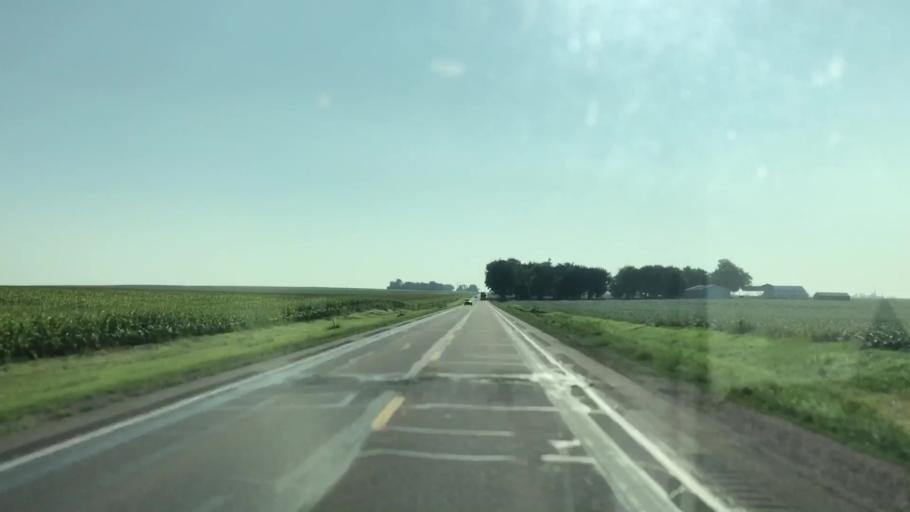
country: US
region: Iowa
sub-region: O'Brien County
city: Sheldon
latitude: 43.1860
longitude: -95.9084
